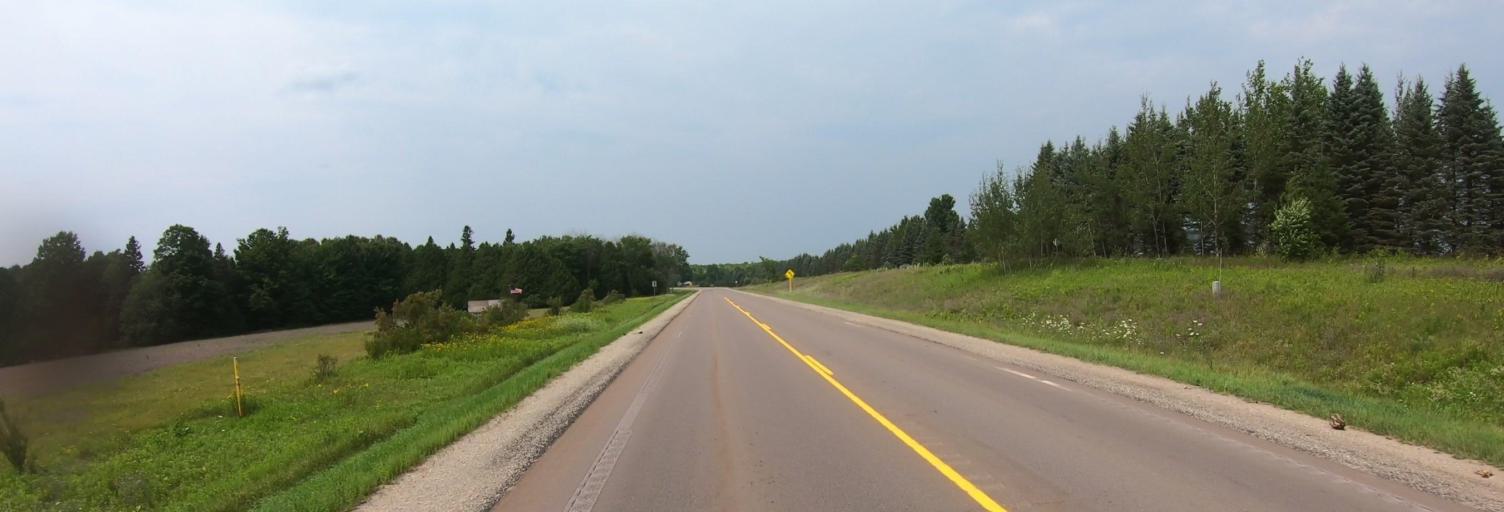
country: US
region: Michigan
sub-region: Alger County
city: Munising
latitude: 46.3499
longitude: -86.9510
